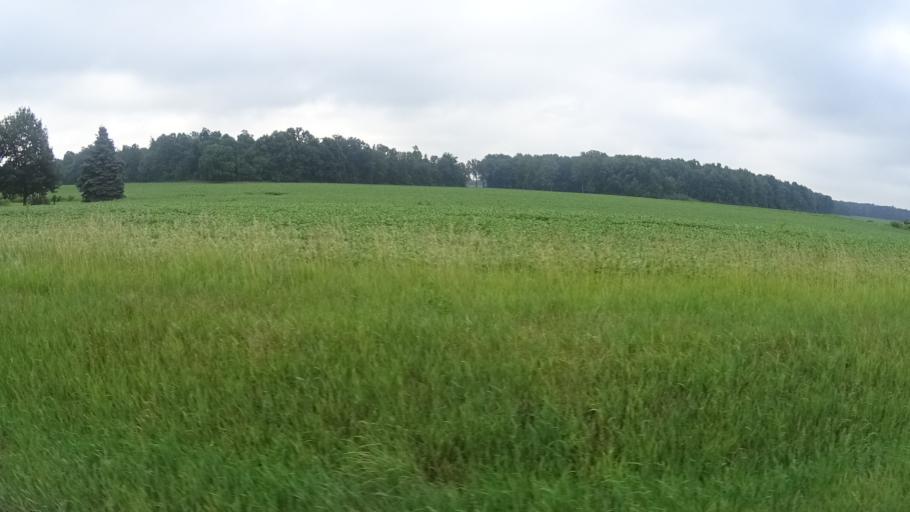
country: US
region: Ohio
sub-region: Erie County
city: Milan
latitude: 41.3003
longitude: -82.5214
